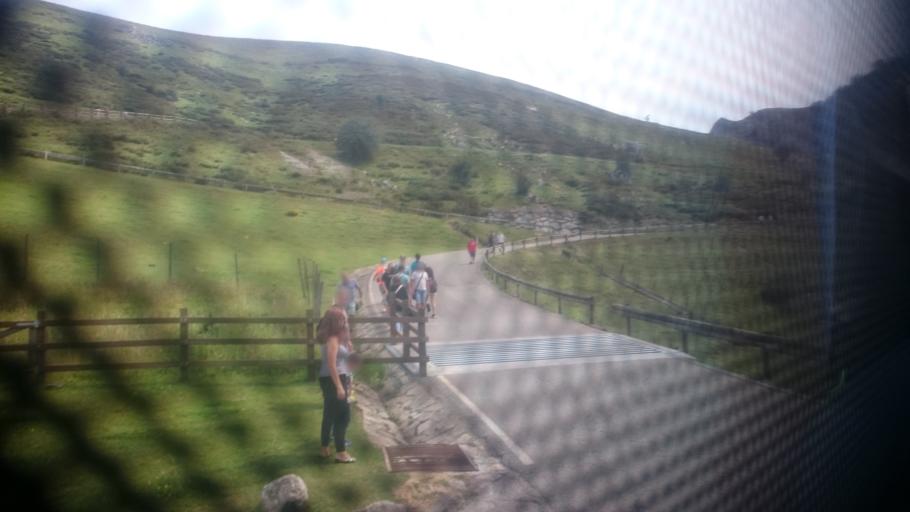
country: ES
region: Asturias
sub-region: Province of Asturias
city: Amieva
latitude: 43.2757
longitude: -4.9861
